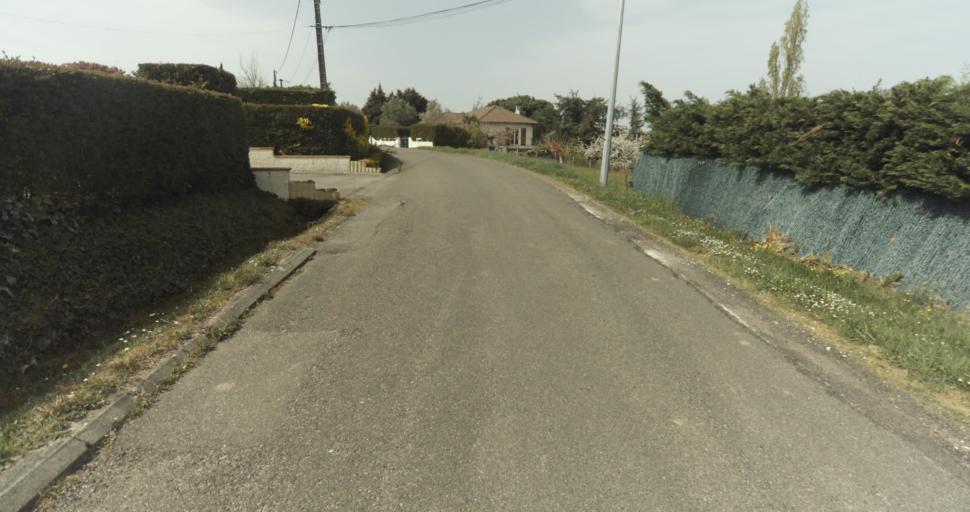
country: FR
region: Midi-Pyrenees
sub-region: Departement du Tarn-et-Garonne
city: Moissac
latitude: 44.1147
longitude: 1.0827
